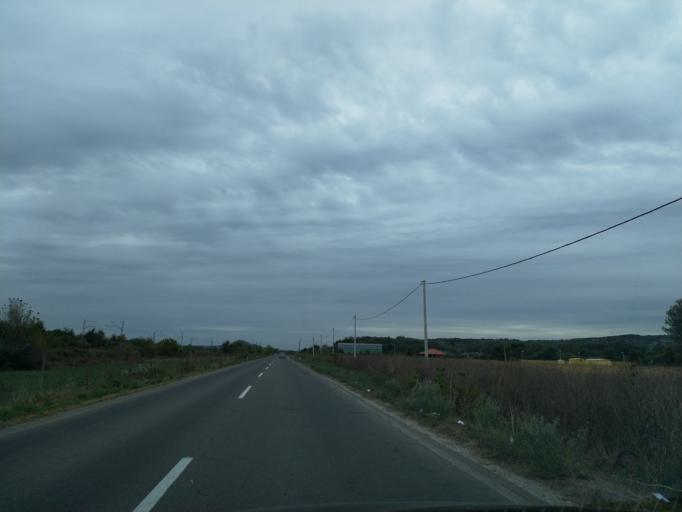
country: RS
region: Central Serbia
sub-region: Sumadijski Okrug
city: Batocina
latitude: 44.1458
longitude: 21.1123
